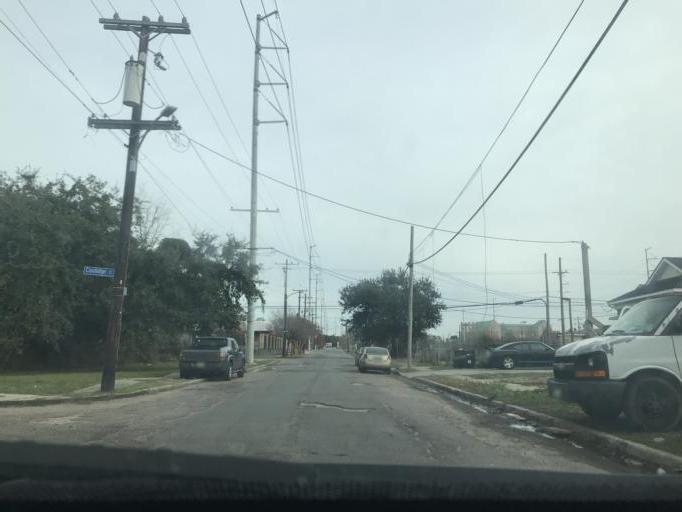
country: US
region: Louisiana
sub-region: Orleans Parish
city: New Orleans
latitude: 29.9608
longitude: -90.1093
